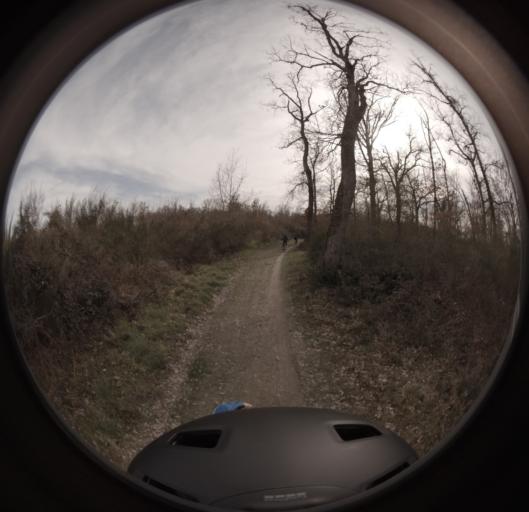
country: FR
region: Midi-Pyrenees
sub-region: Departement du Tarn-et-Garonne
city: Montech
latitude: 43.9579
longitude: 1.2591
